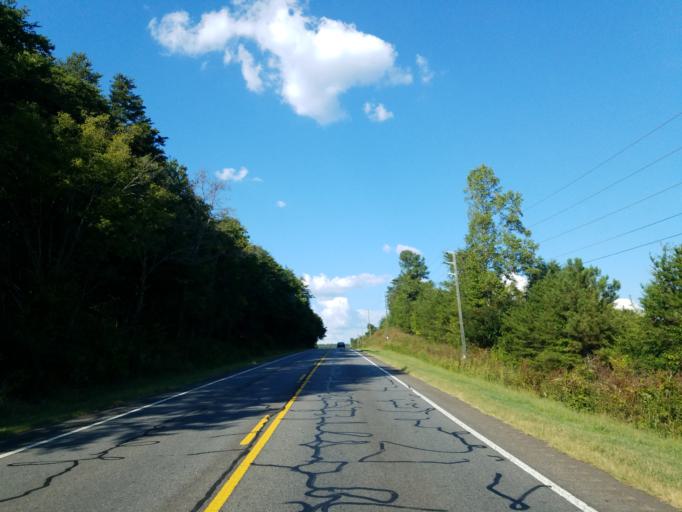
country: US
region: Georgia
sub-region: Bartow County
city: Rydal
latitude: 34.3718
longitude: -84.7114
